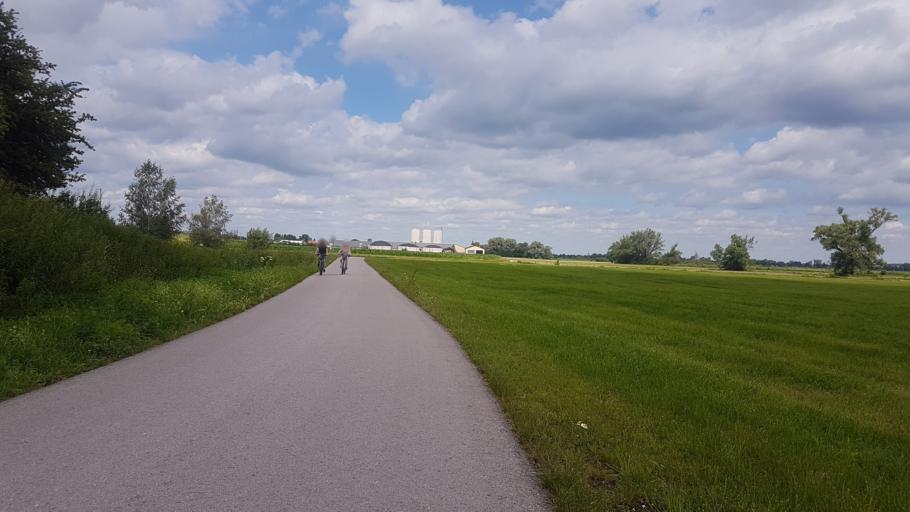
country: DE
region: Bavaria
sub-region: Regierungsbezirk Mittelfranken
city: Gunzenhausen
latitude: 49.0877
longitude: 10.7657
